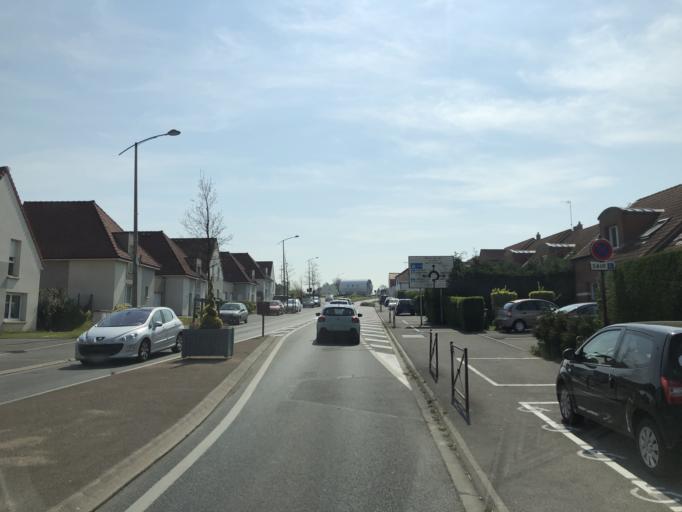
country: FR
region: Nord-Pas-de-Calais
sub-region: Departement du Pas-de-Calais
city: Coquelles
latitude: 50.9309
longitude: 1.7986
